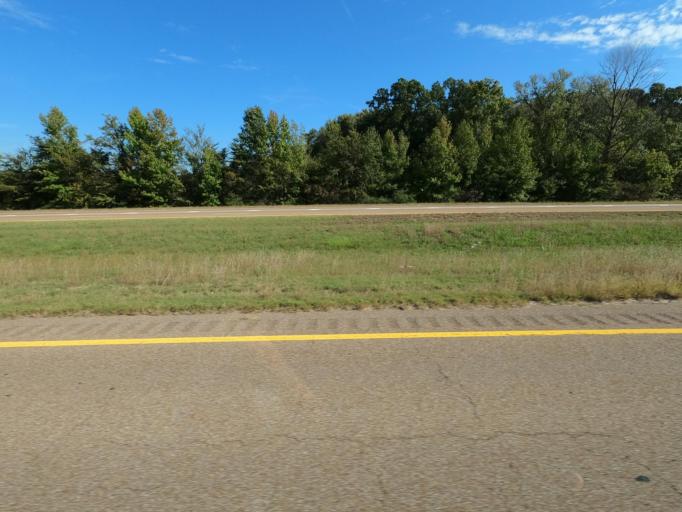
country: US
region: Tennessee
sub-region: Shelby County
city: Millington
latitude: 35.3218
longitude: -89.8777
